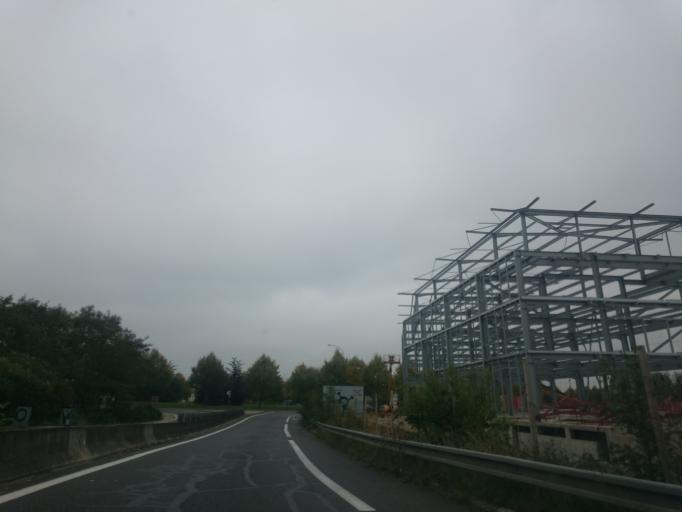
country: FR
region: Ile-de-France
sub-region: Departement de l'Essonne
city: Grigny
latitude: 48.6488
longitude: 2.3874
